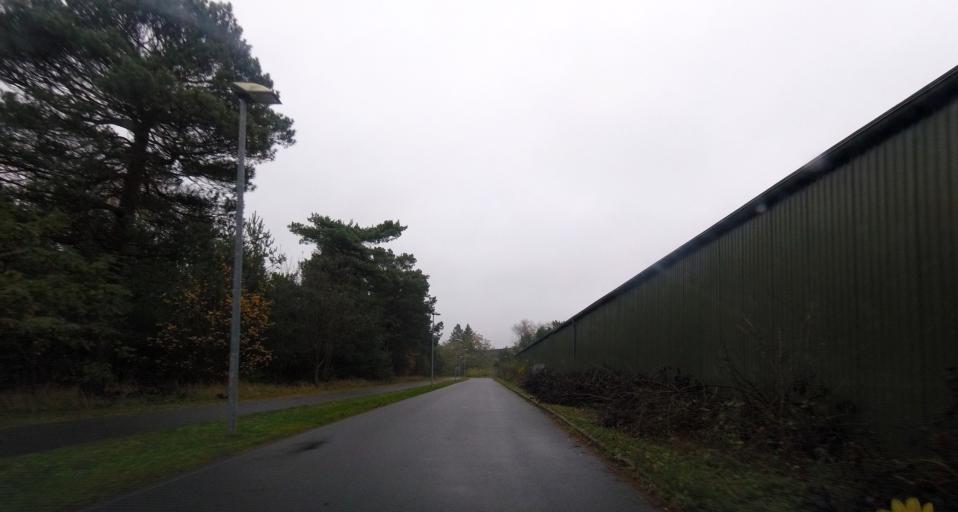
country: DE
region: Brandenburg
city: Niedergorsdorf
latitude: 52.0021
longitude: 12.9921
